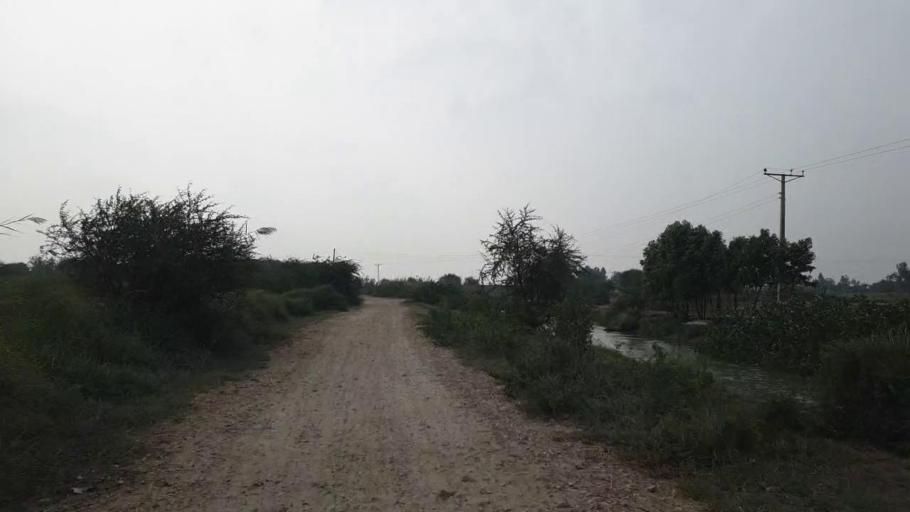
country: PK
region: Sindh
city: Kario
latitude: 24.8647
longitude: 68.5184
